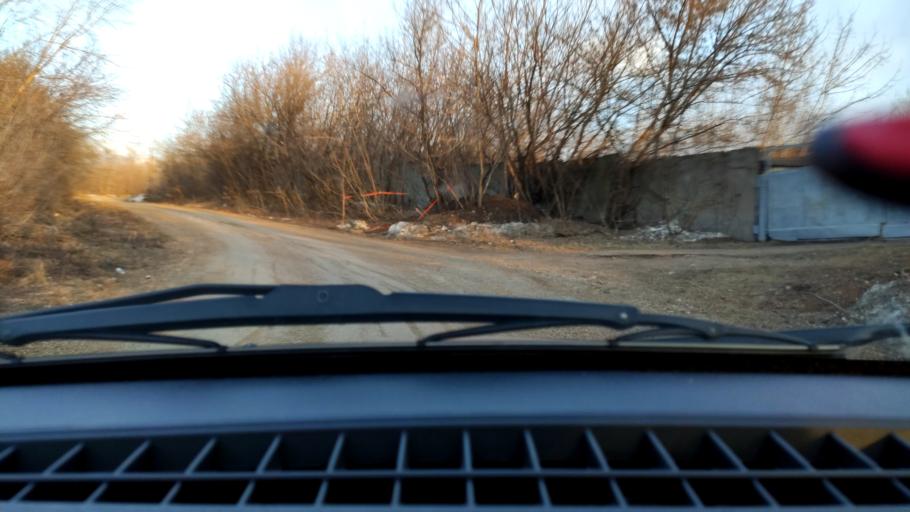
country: RU
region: Bashkortostan
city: Ufa
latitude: 54.8360
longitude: 56.0725
